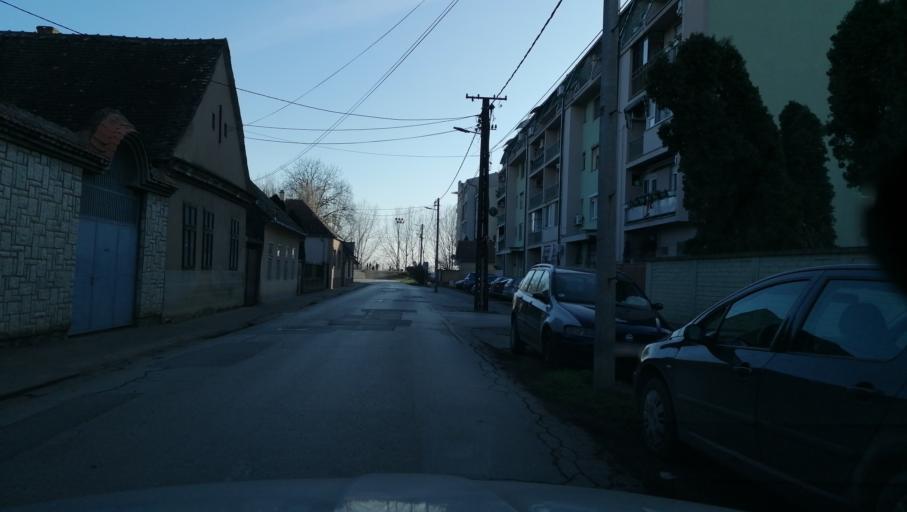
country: RS
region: Autonomna Pokrajina Vojvodina
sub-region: Sremski Okrug
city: Sremska Mitrovica
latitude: 44.9637
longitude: 19.6129
